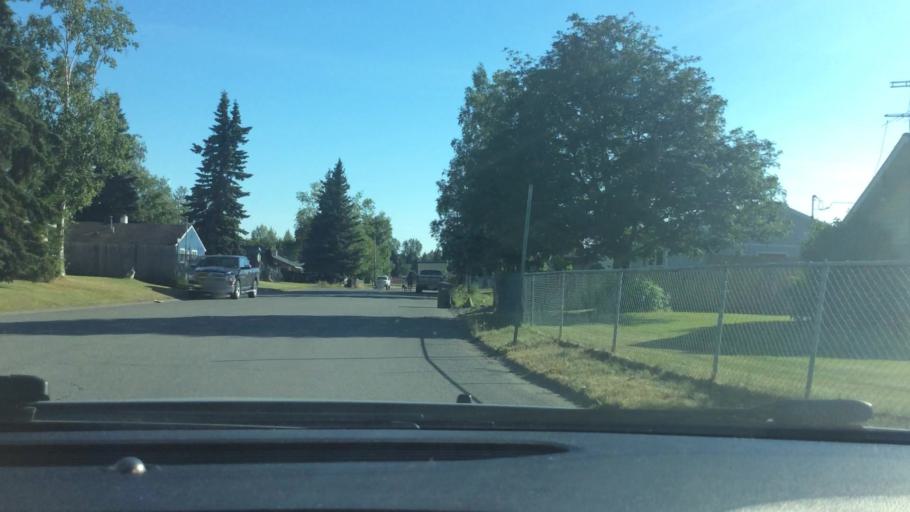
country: US
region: Alaska
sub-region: Anchorage Municipality
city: Anchorage
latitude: 61.2058
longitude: -149.7710
